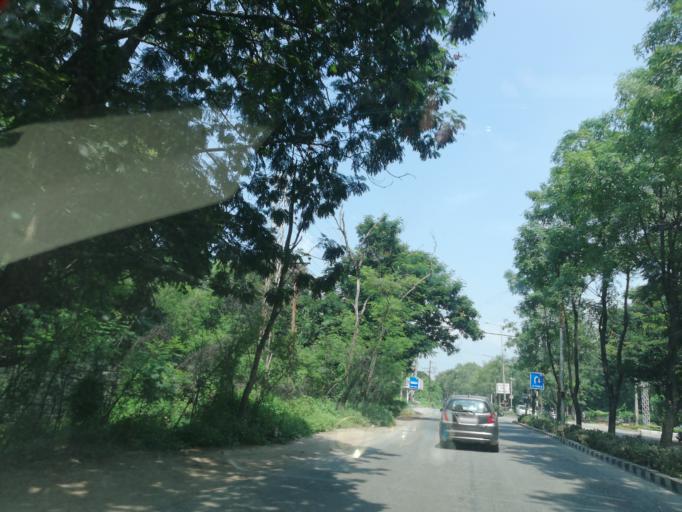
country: IN
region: Telangana
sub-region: Medak
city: Serilingampalle
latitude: 17.4596
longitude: 78.3377
